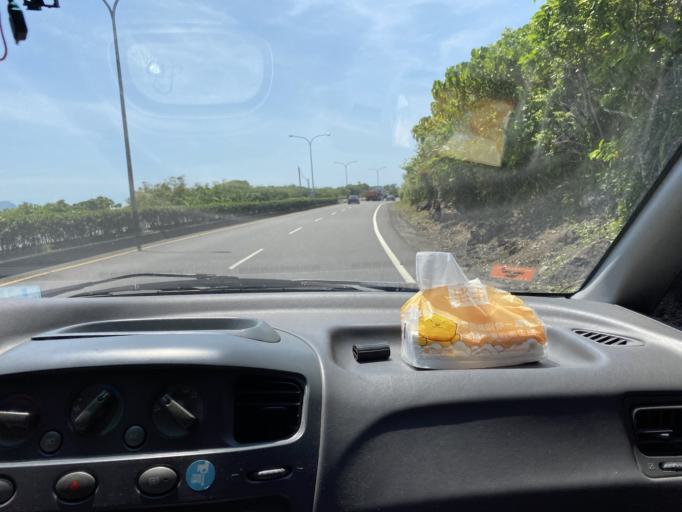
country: TW
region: Taiwan
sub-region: Yilan
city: Yilan
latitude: 24.9277
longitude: 121.8860
